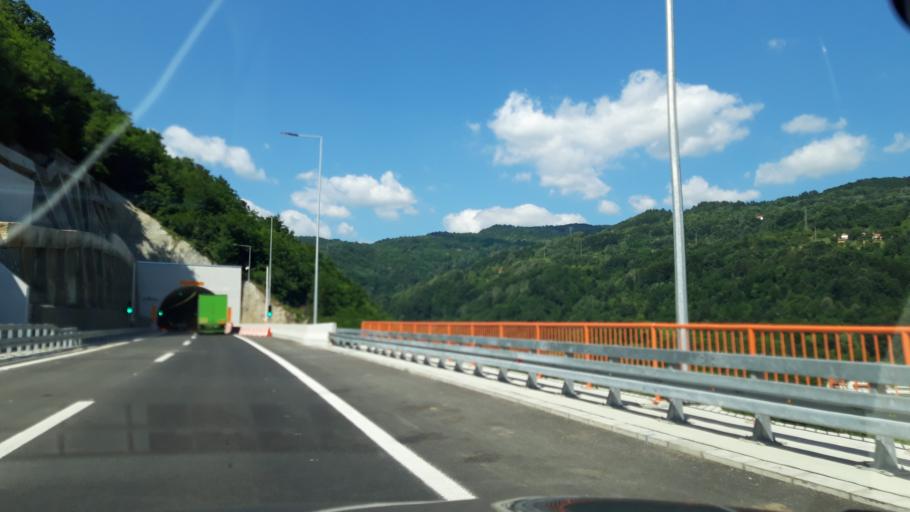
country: RS
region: Central Serbia
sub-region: Jablanicki Okrug
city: Vlasotince
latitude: 42.8349
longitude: 22.1294
